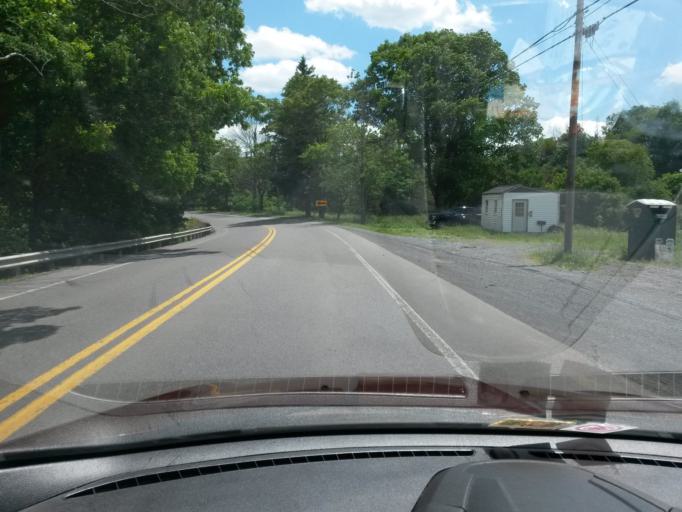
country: US
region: West Virginia
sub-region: Greenbrier County
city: Rainelle
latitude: 37.9251
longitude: -80.6478
